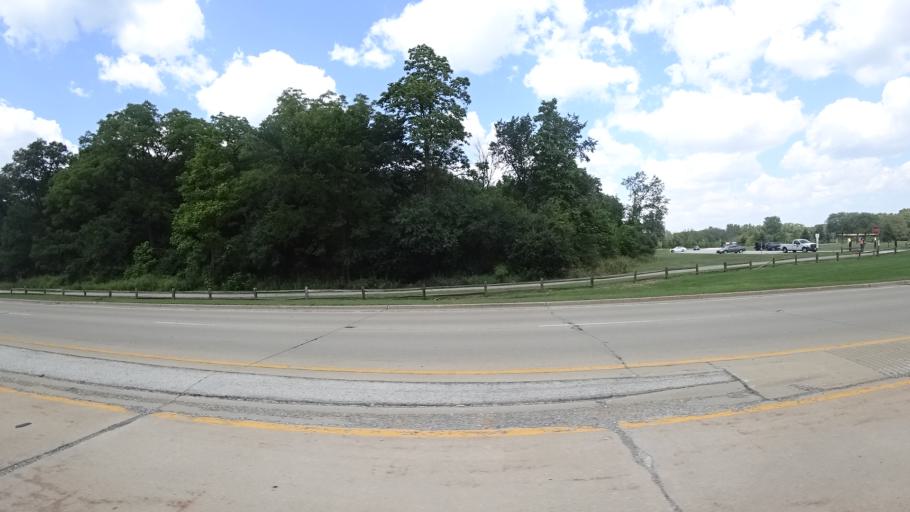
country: US
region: Illinois
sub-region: Cook County
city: Crestwood
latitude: 41.6321
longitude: -87.7666
